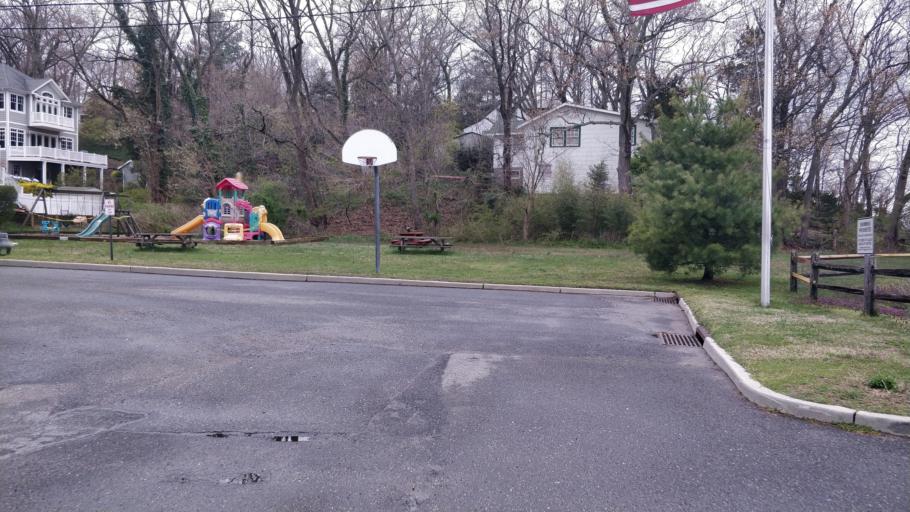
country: US
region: New York
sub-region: Suffolk County
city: Port Jefferson
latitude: 40.9529
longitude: -73.0821
